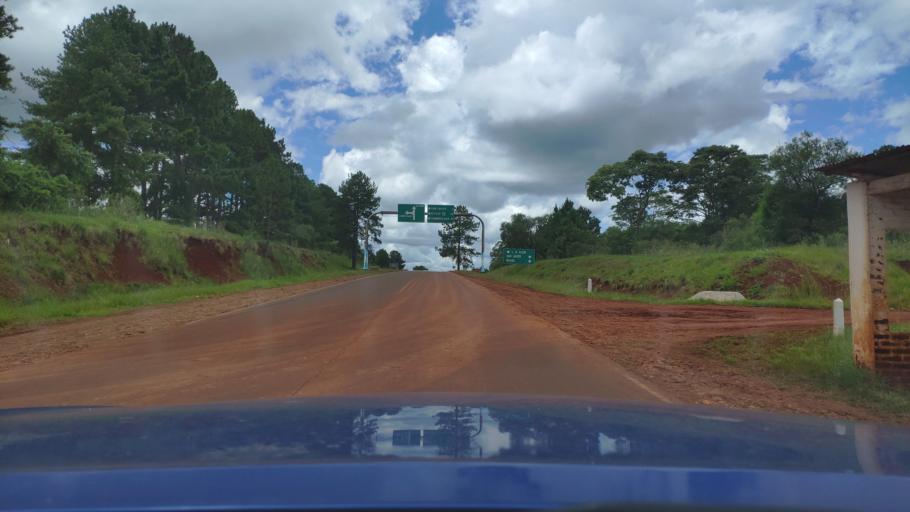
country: AR
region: Misiones
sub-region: Departamento de San Javier
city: San Javier
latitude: -27.8394
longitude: -55.2230
